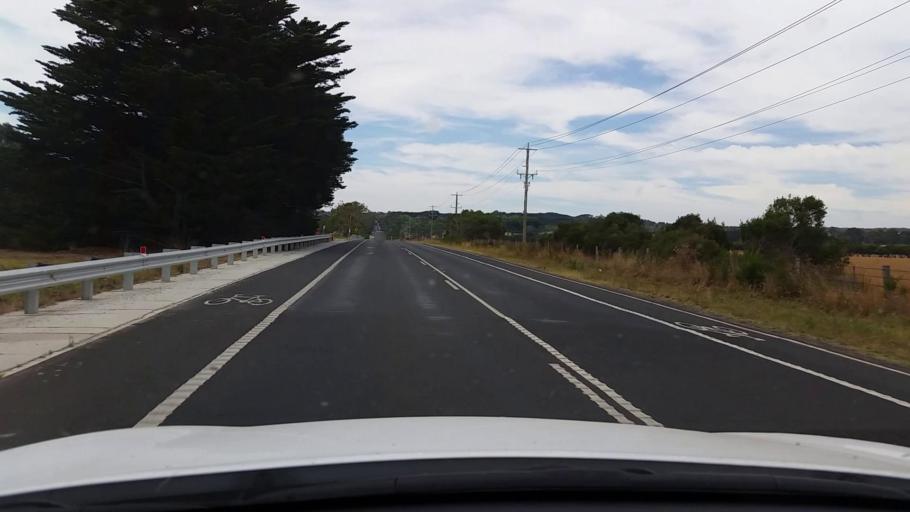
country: AU
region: Victoria
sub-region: Mornington Peninsula
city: Safety Beach
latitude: -38.3139
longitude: 145.0218
